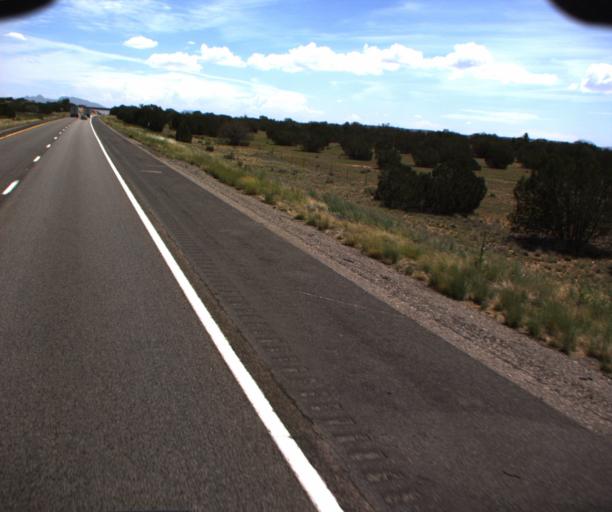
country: US
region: Arizona
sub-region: Mohave County
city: Peach Springs
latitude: 35.3177
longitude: -112.9562
